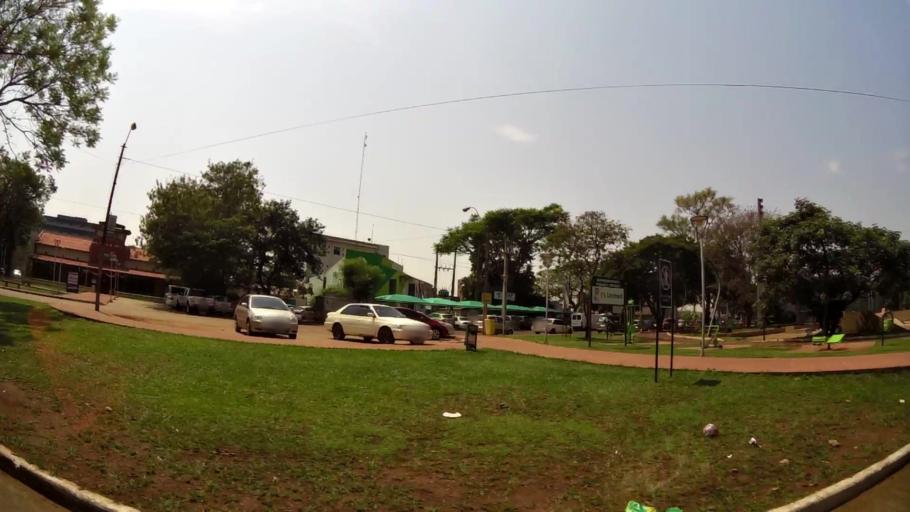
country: PY
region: Alto Parana
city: Ciudad del Este
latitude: -25.5202
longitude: -54.6129
